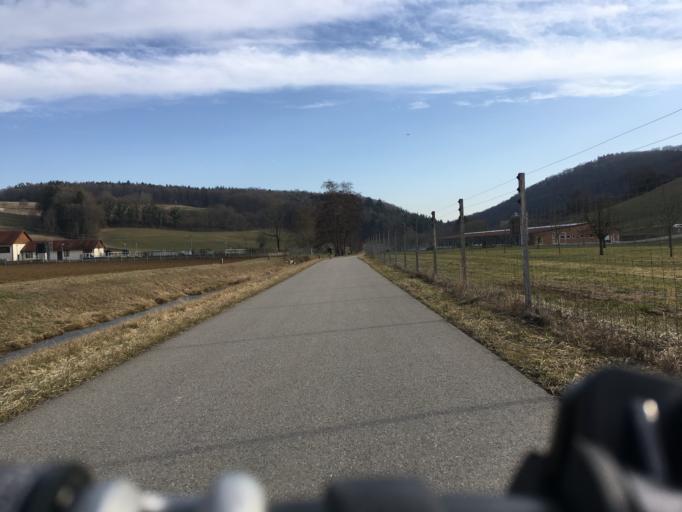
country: CH
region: Schaffhausen
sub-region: Bezirk Reiat
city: Thayngen
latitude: 47.7679
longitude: 8.6853
